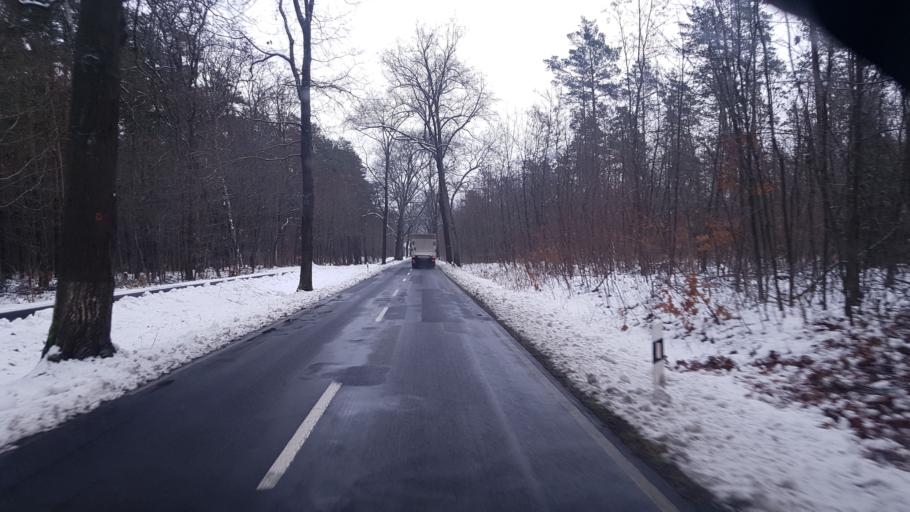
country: DE
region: Brandenburg
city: Lawitz
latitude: 52.0816
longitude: 14.5244
